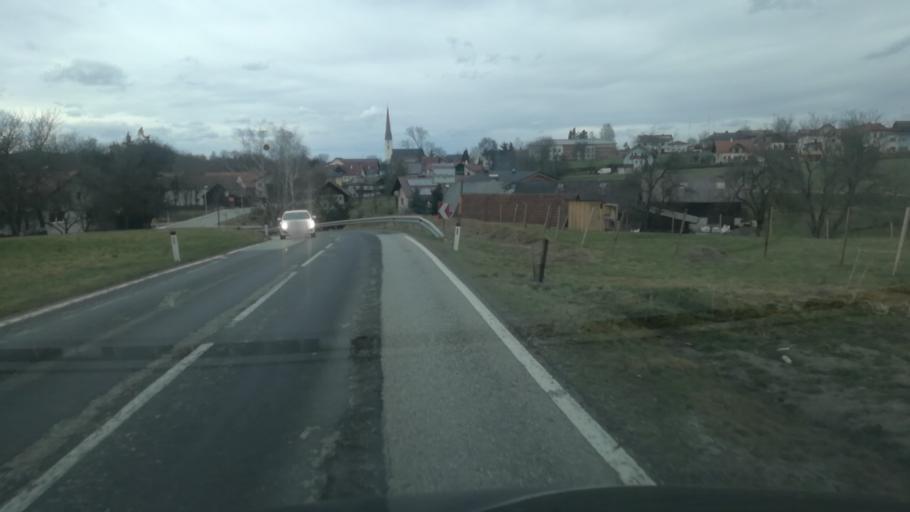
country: AT
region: Upper Austria
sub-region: Politischer Bezirk Ried im Innkreis
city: Ried im Innkreis
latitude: 48.1505
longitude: 13.4868
